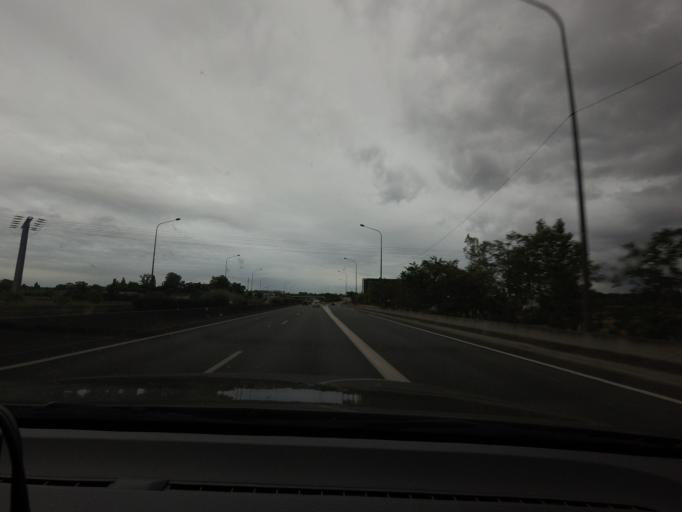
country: FR
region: Midi-Pyrenees
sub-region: Departement de la Haute-Garonne
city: Colomiers
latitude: 43.5998
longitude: 1.3648
